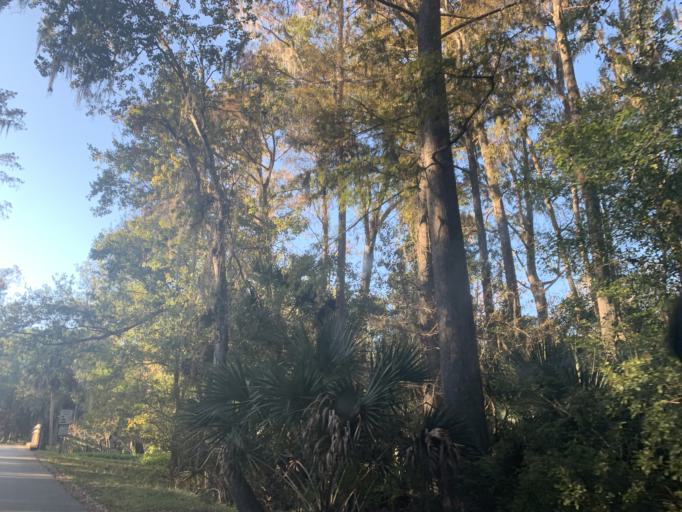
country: US
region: Florida
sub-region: Pinellas County
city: East Lake
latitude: 28.0926
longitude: -82.7061
